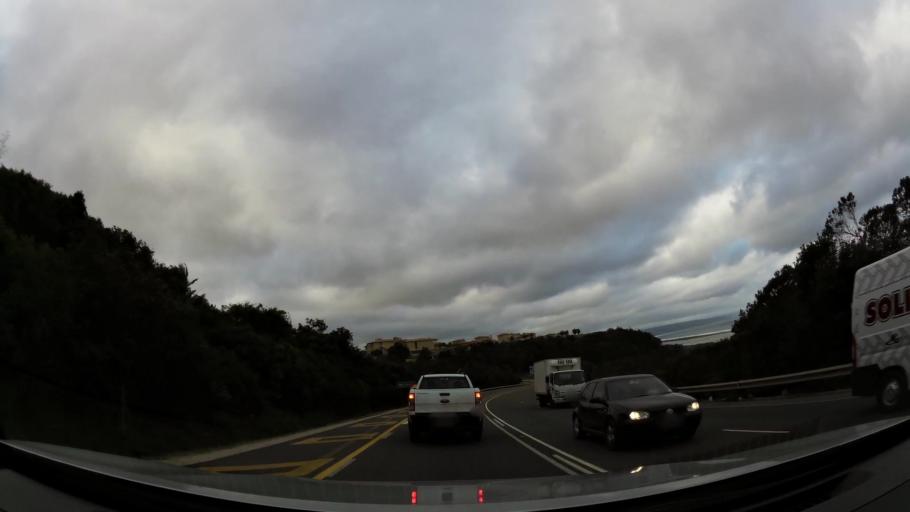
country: ZA
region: Western Cape
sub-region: Eden District Municipality
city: Plettenberg Bay
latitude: -34.0457
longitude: 23.3619
